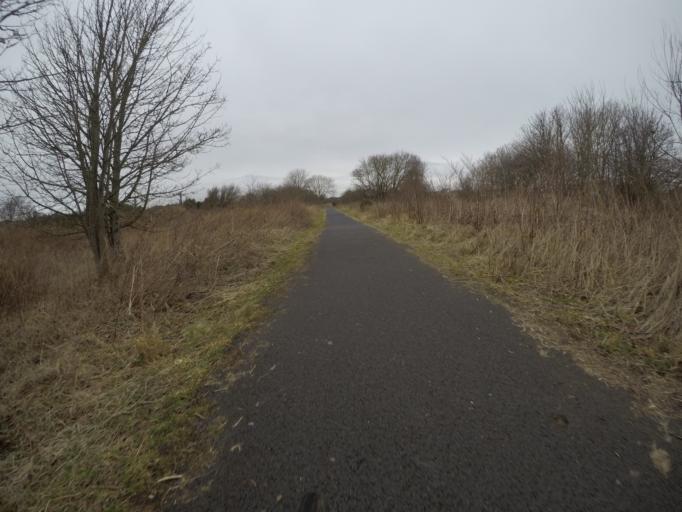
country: GB
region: Scotland
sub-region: North Ayrshire
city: Irvine
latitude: 55.6277
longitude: -4.6859
